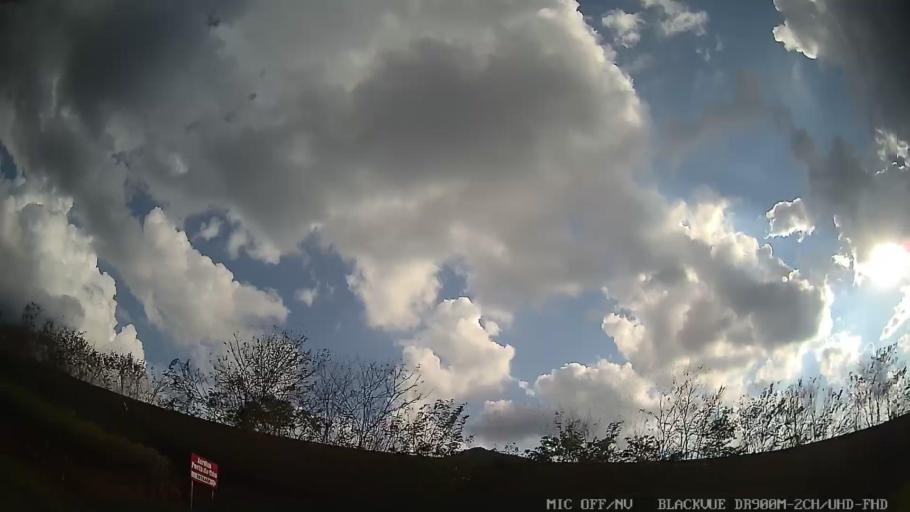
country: BR
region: Sao Paulo
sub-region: Braganca Paulista
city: Braganca Paulista
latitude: -22.9097
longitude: -46.4716
